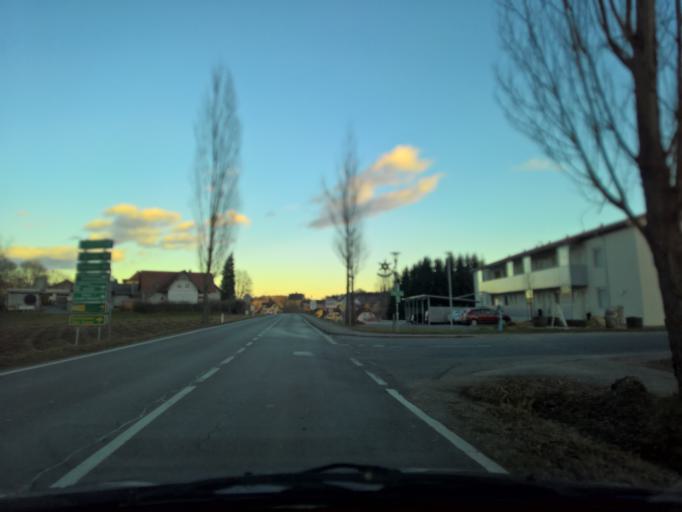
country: AT
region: Styria
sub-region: Politischer Bezirk Leibnitz
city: Gamlitz
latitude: 46.7185
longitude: 15.5459
